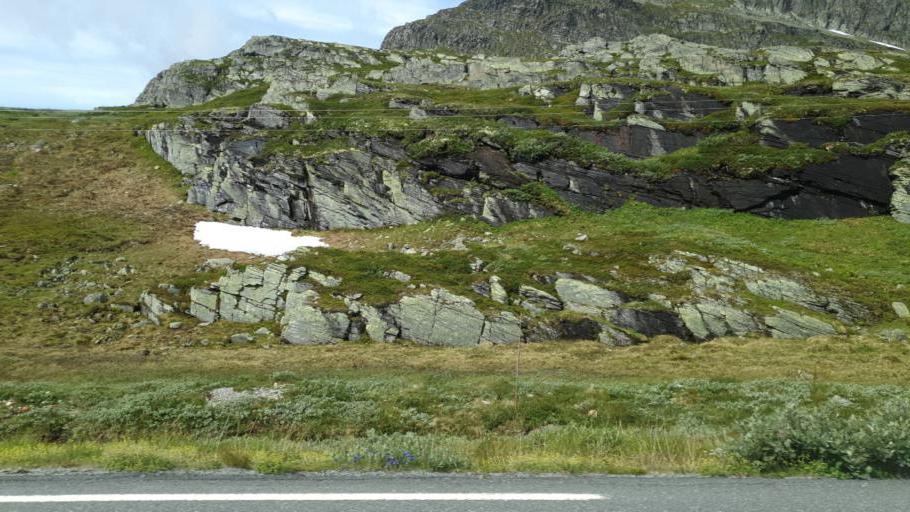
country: NO
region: Oppland
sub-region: Vestre Slidre
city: Slidre
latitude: 61.2919
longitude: 8.8136
